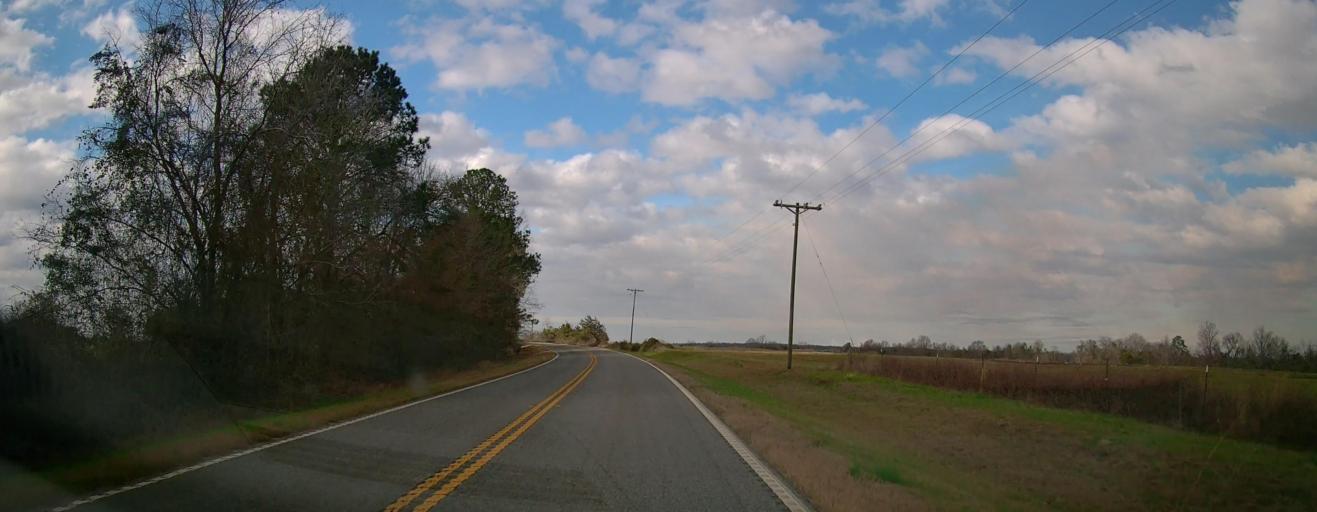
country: US
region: Georgia
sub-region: Marion County
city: Buena Vista
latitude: 32.4469
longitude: -84.4406
